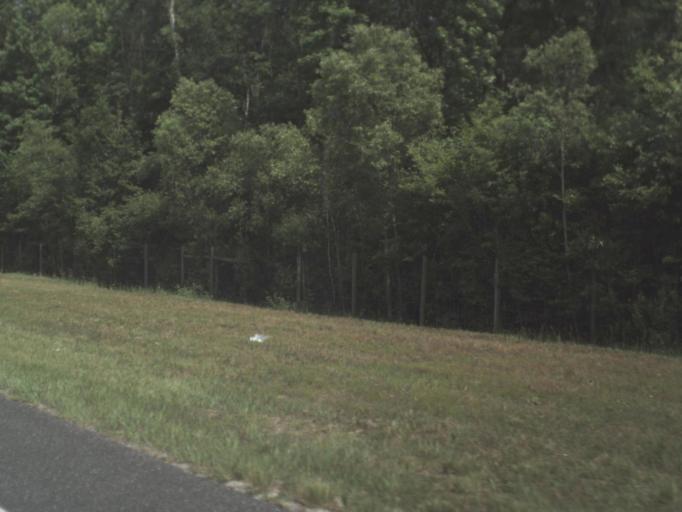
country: US
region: Florida
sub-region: Putnam County
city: Interlachen
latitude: 29.6280
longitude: -81.7710
